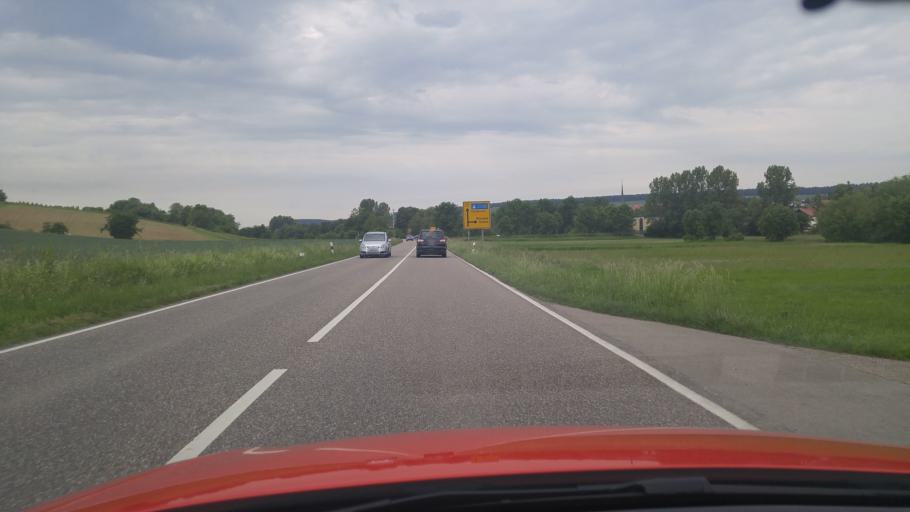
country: DE
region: Baden-Wuerttemberg
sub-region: Regierungsbezirk Stuttgart
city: Lehrensteinsfeld
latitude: 49.1420
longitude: 9.3447
